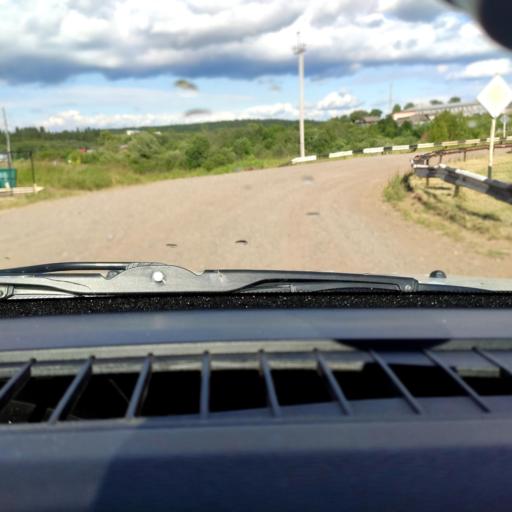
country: RU
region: Perm
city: Uinskoye
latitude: 57.1195
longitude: 56.5197
